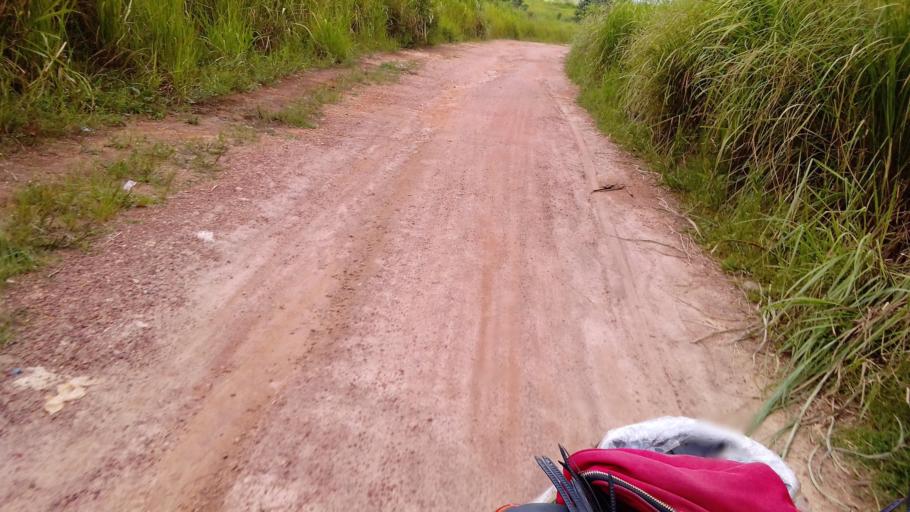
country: SL
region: Eastern Province
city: Koidu
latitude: 8.6829
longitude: -10.9575
